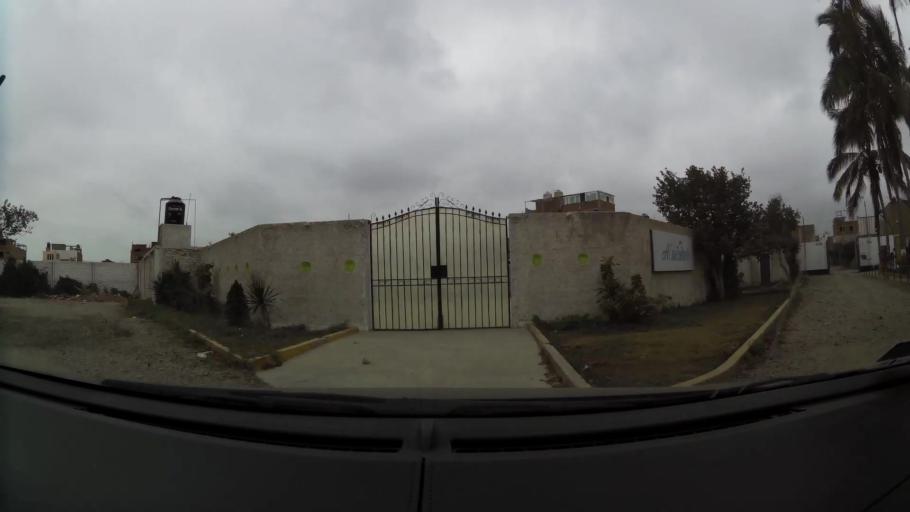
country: PE
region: La Libertad
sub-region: Provincia de Trujillo
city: Trujillo
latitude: -8.1216
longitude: -79.0450
